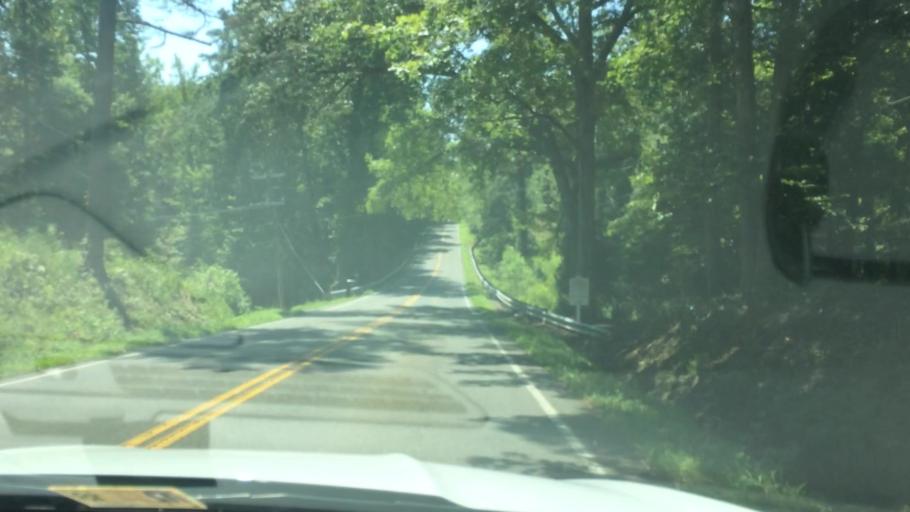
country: US
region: Virginia
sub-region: Charles City County
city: Charles City
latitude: 37.4054
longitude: -77.0469
